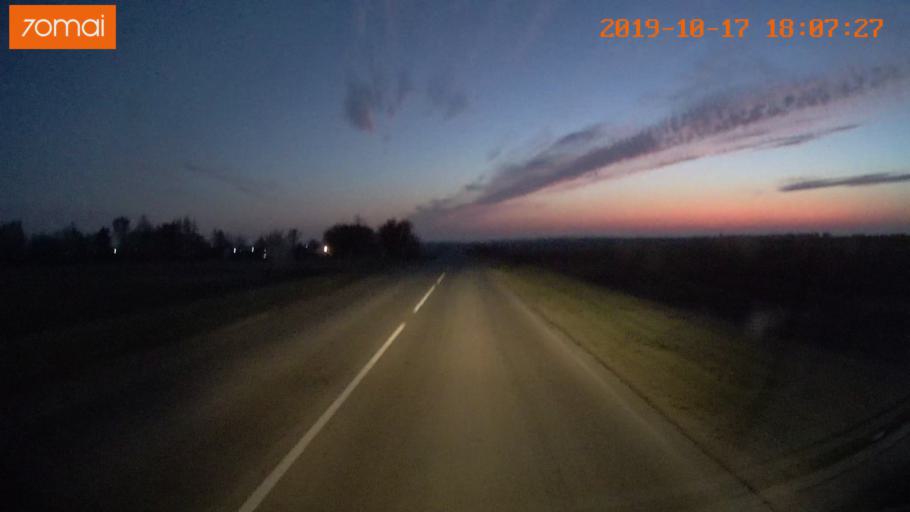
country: RU
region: Tula
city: Kurkino
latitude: 53.4438
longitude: 38.6546
